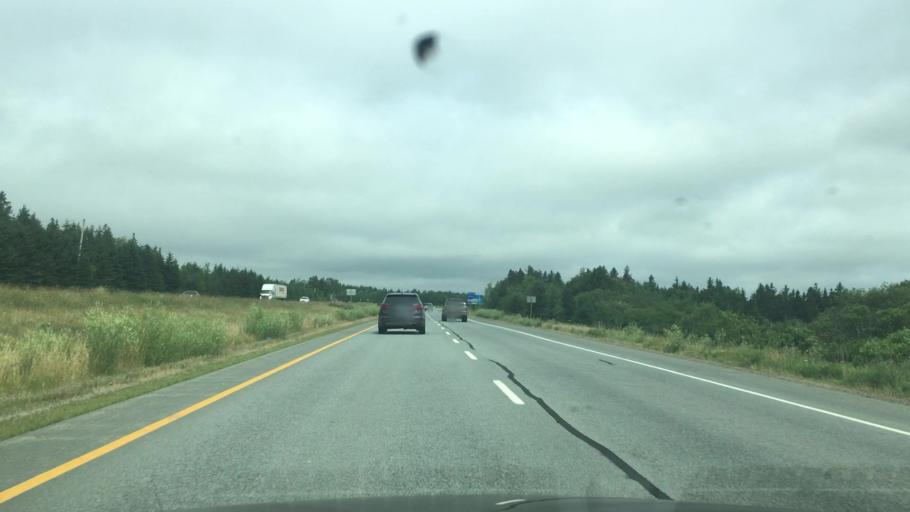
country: CA
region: Nova Scotia
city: Truro
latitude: 45.2978
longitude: -63.3025
